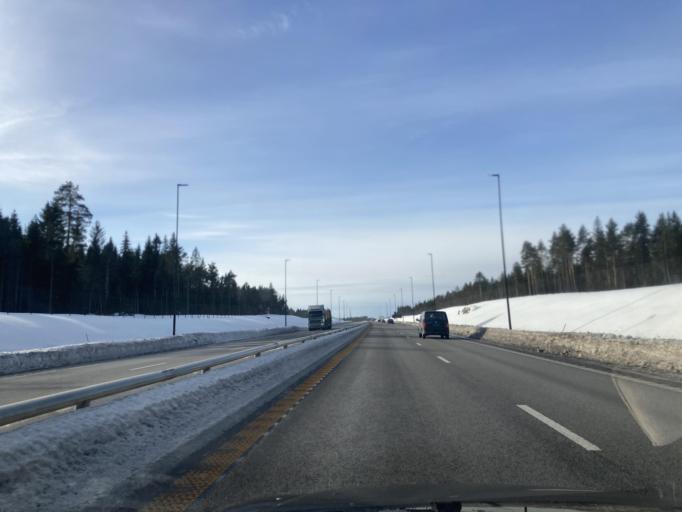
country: NO
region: Hedmark
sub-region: Loten
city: Loten
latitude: 60.8587
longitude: 11.4070
